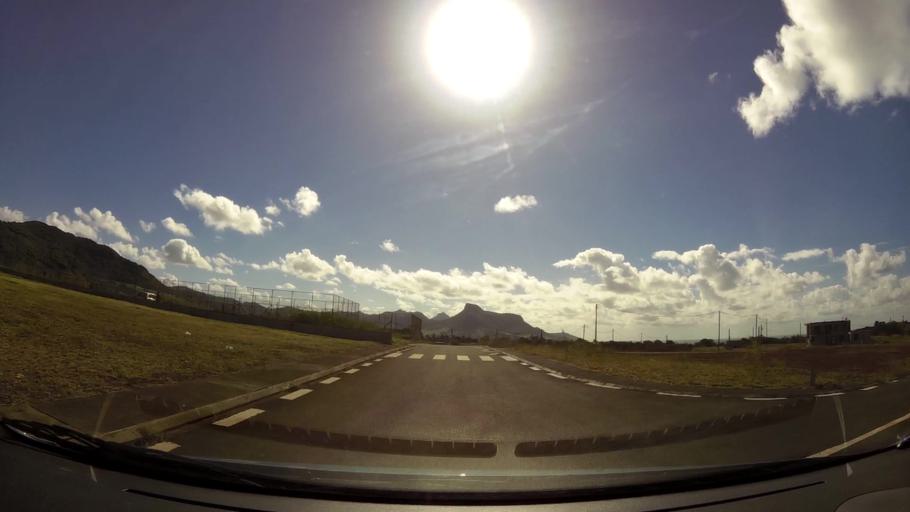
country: MU
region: Grand Port
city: Mahebourg
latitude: -20.4060
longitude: 57.6914
